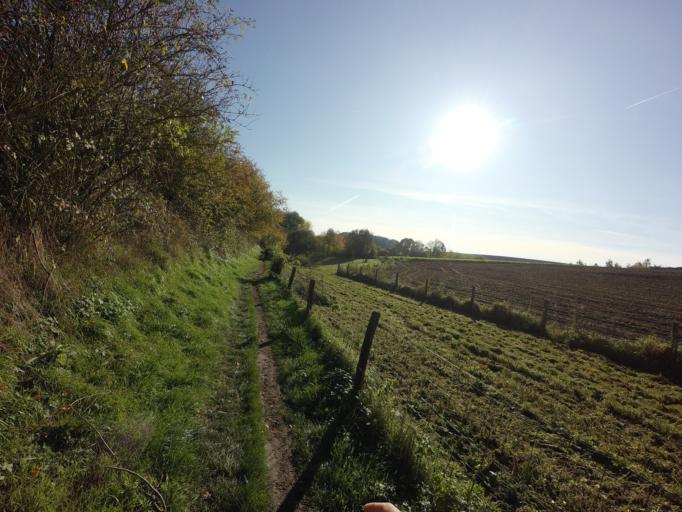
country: NL
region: Limburg
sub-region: Gemeente Voerendaal
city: Ubachsberg
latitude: 50.8347
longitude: 5.9511
